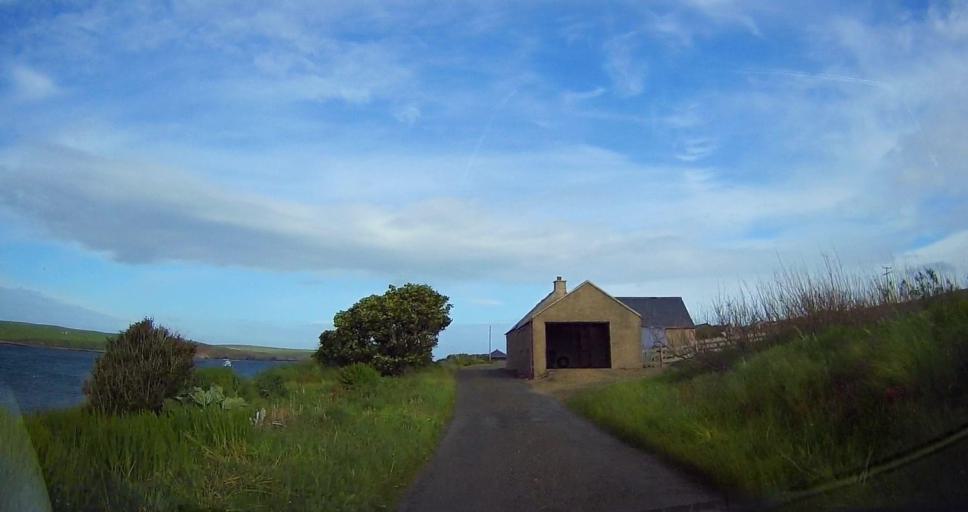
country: GB
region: Scotland
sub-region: Orkney Islands
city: Stromness
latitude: 58.7810
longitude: -3.2345
